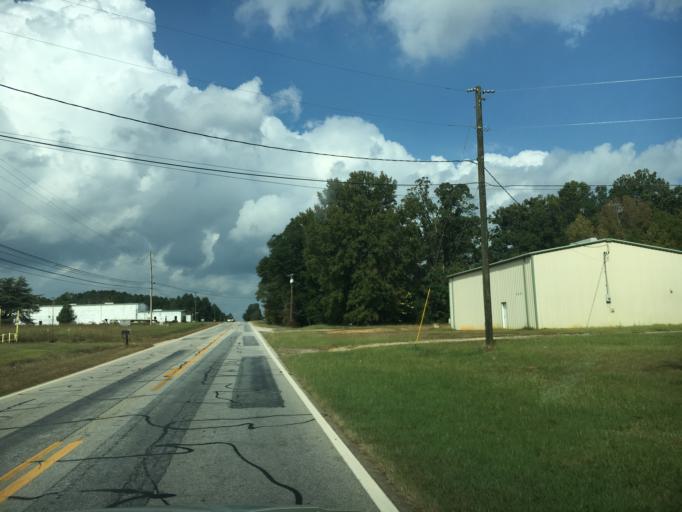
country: US
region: Georgia
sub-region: Elbert County
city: Elberton
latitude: 34.2050
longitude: -82.8917
